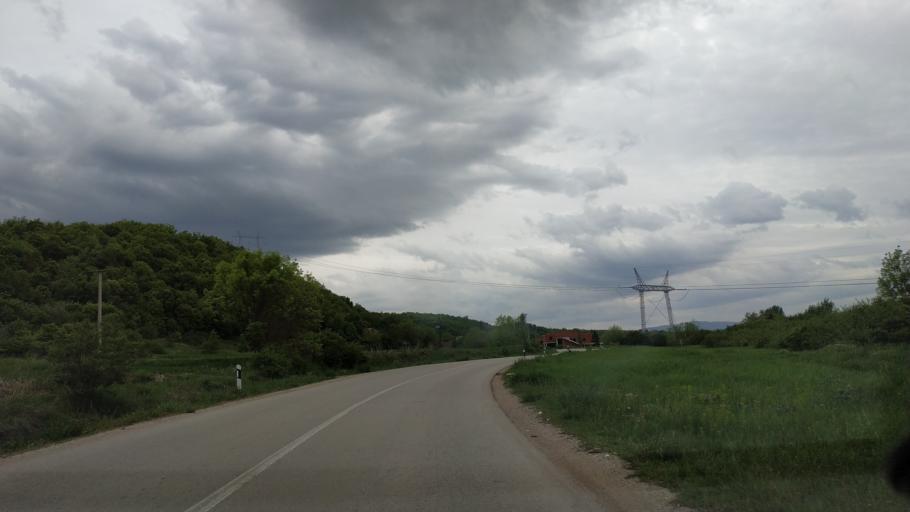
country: RS
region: Central Serbia
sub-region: Nisavski Okrug
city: Aleksinac
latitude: 43.6245
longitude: 21.6921
